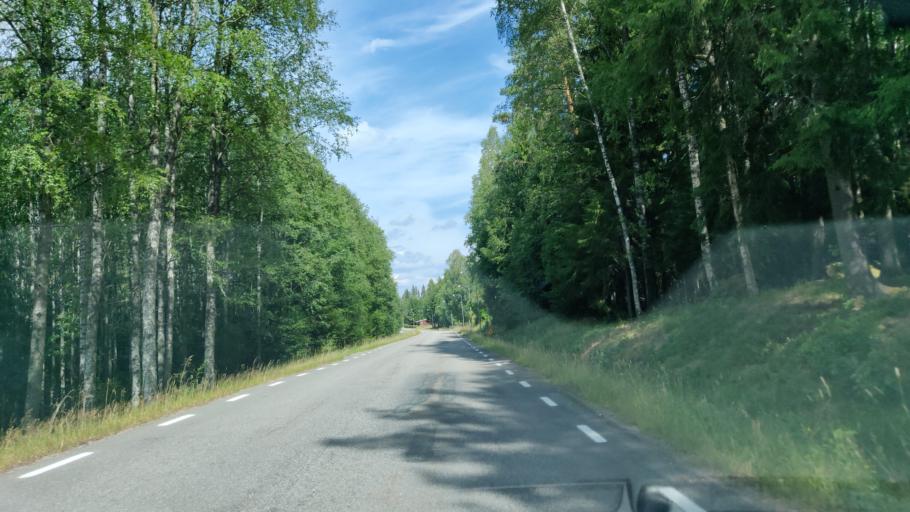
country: SE
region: Vaermland
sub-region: Hagfors Kommun
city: Ekshaerad
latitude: 60.1077
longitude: 13.5008
